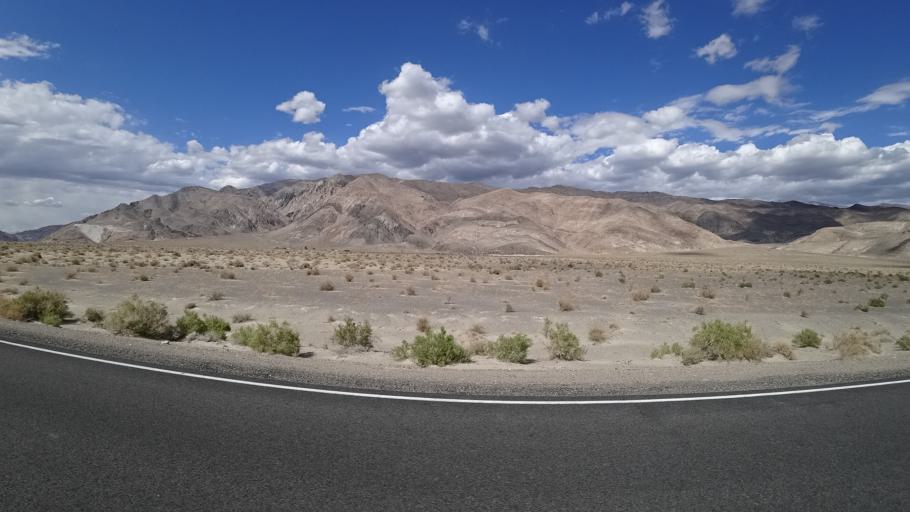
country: US
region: California
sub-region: Inyo County
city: Lone Pine
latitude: 36.5481
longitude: -117.9452
